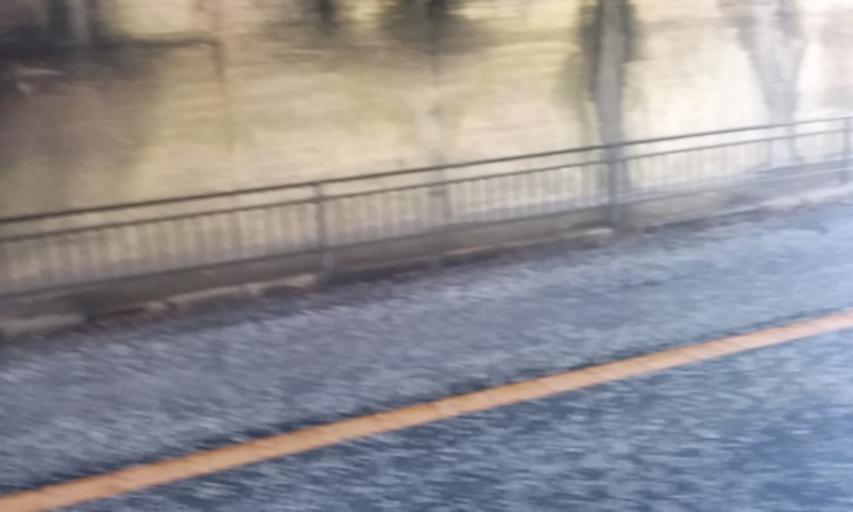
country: JP
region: Kanagawa
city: Kamakura
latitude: 35.3197
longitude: 139.5458
